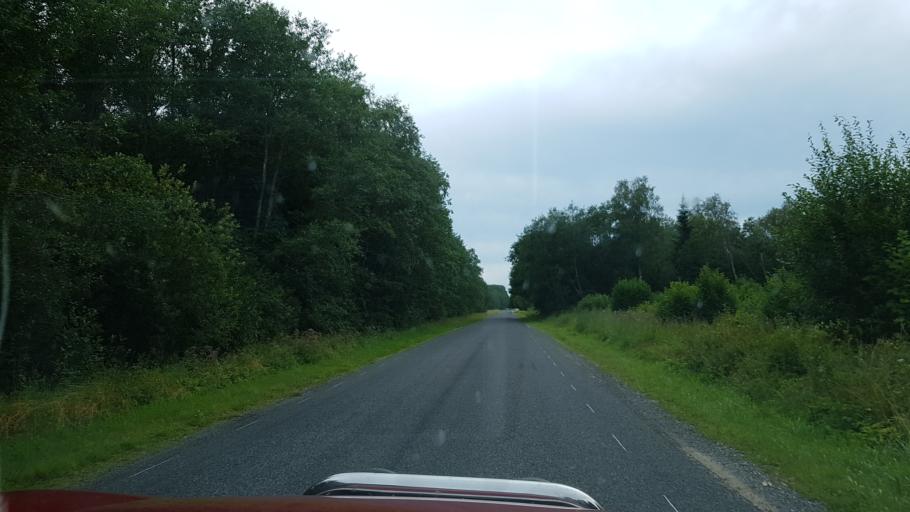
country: EE
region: Laeaene
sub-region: Lihula vald
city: Lihula
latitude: 58.8643
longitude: 23.8307
